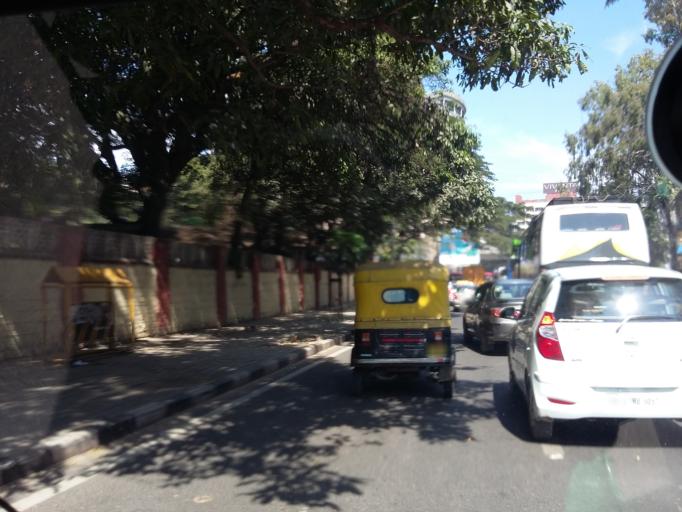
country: IN
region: Karnataka
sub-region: Bangalore Urban
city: Bangalore
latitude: 12.9705
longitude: 77.6196
